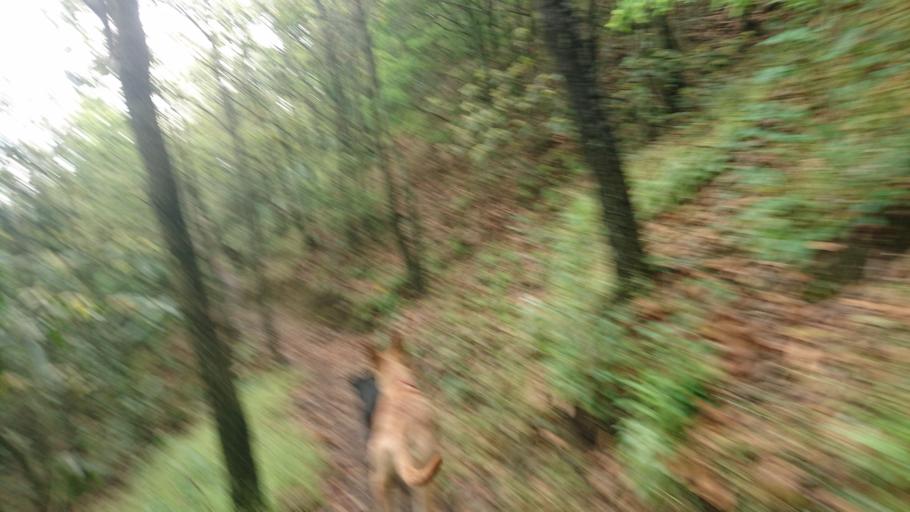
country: MX
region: Nuevo Leon
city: Garza Garcia
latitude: 25.6041
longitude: -100.3374
